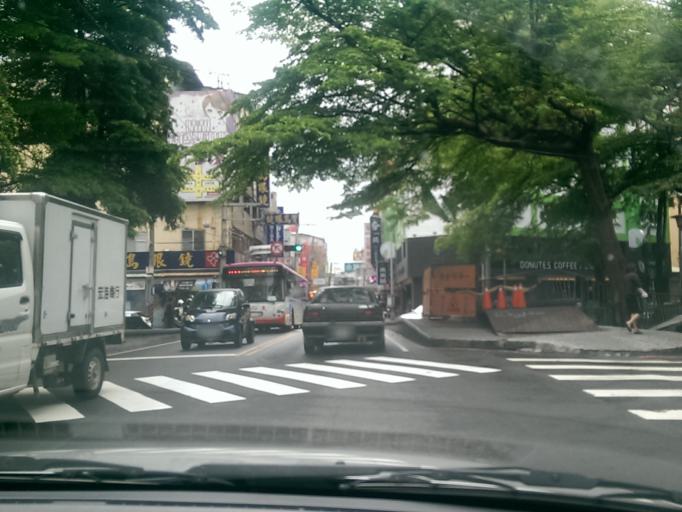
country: TW
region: Taiwan
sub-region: Taichung City
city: Taichung
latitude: 24.1775
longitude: 120.6428
